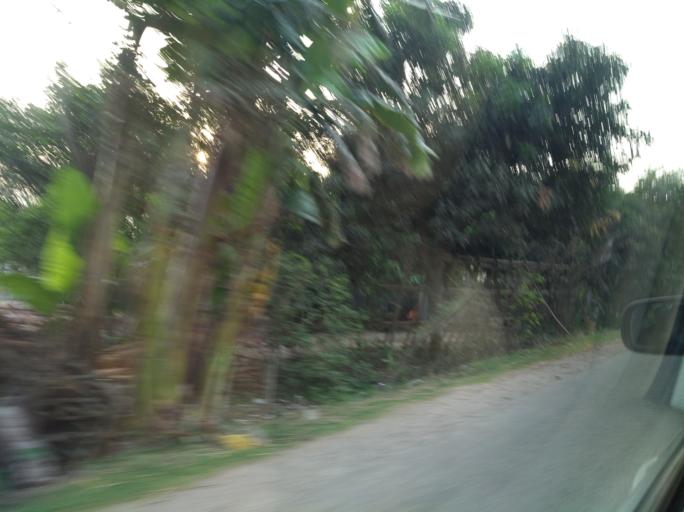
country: BD
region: Rajshahi
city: Bogra
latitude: 24.7035
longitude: 89.3986
